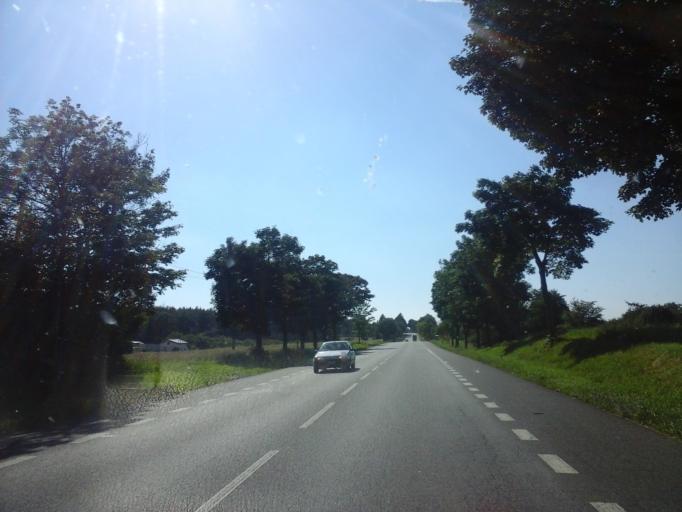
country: PL
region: West Pomeranian Voivodeship
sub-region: Powiat kolobrzeski
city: Ryman
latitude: 53.9645
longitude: 15.6126
